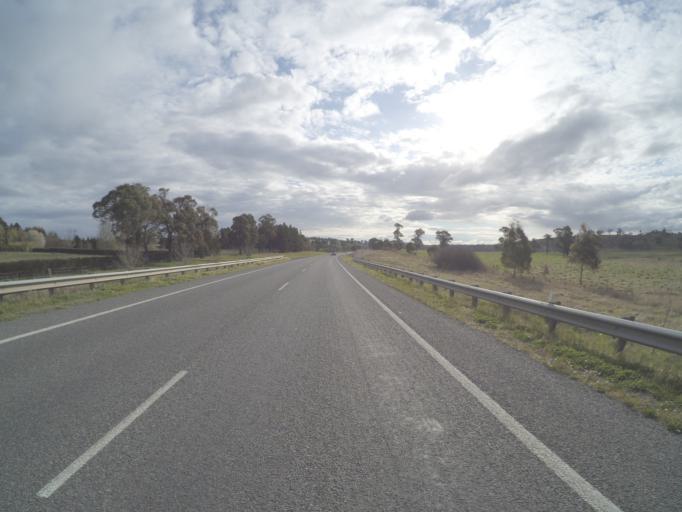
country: AU
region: New South Wales
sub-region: Wingecarribee
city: Bundanoon
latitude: -34.5861
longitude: 150.2705
